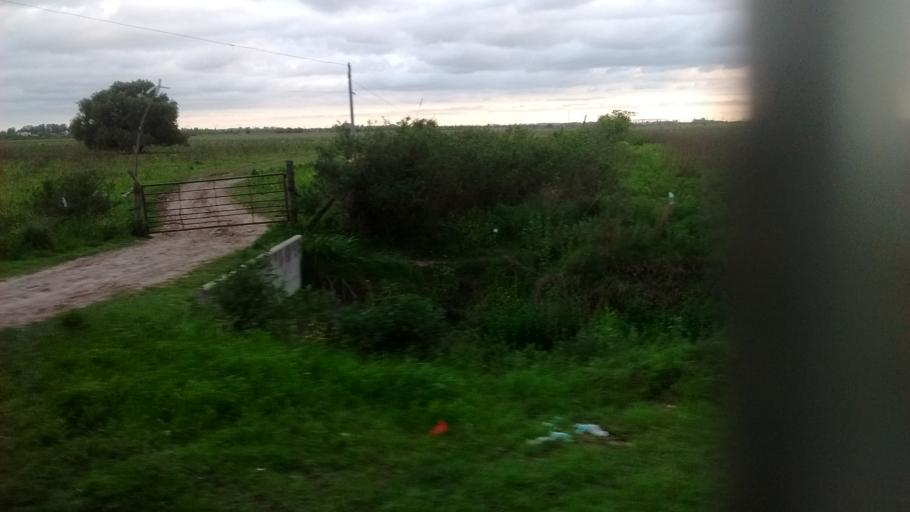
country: AR
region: Santa Fe
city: Funes
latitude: -32.9278
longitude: -60.7723
